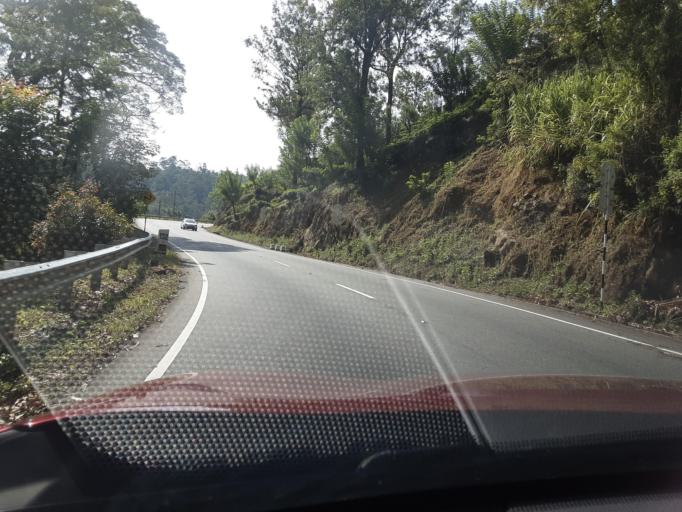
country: LK
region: Uva
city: Badulla
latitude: 6.9596
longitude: 81.1148
